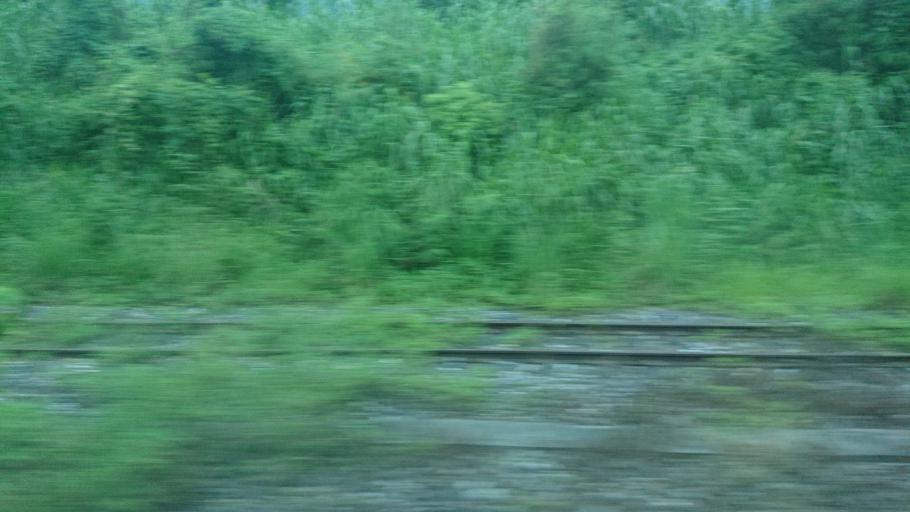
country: TW
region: Taiwan
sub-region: Hualien
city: Hualian
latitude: 24.1237
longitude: 121.6382
